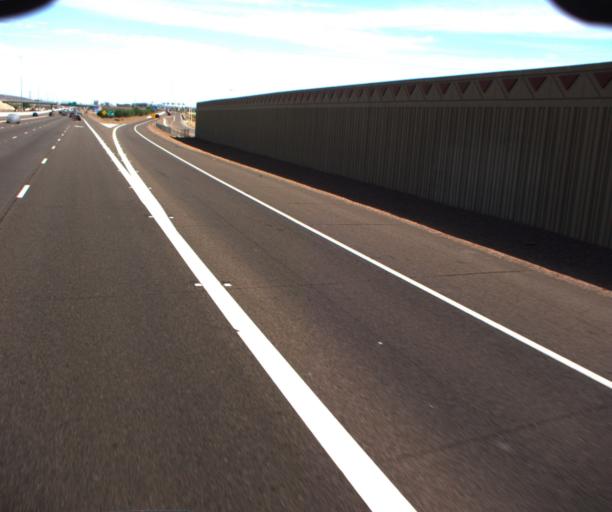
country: US
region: Arizona
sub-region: Maricopa County
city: Peoria
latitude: 33.6952
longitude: -112.1135
